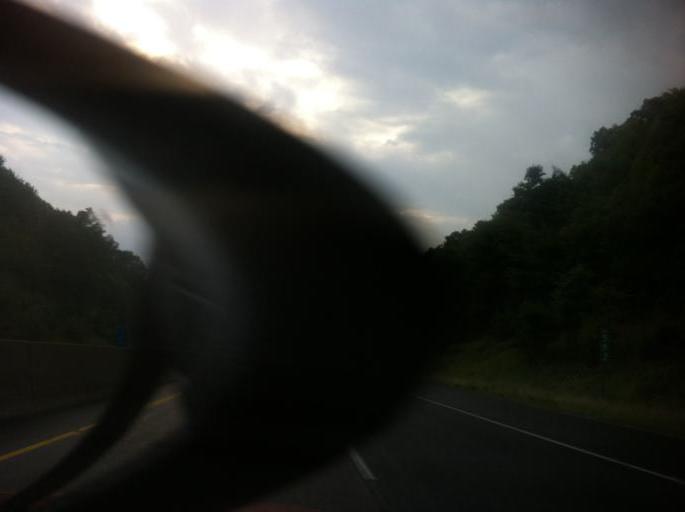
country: US
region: Pennsylvania
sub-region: Clarion County
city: Marianne
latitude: 41.1969
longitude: -79.4634
